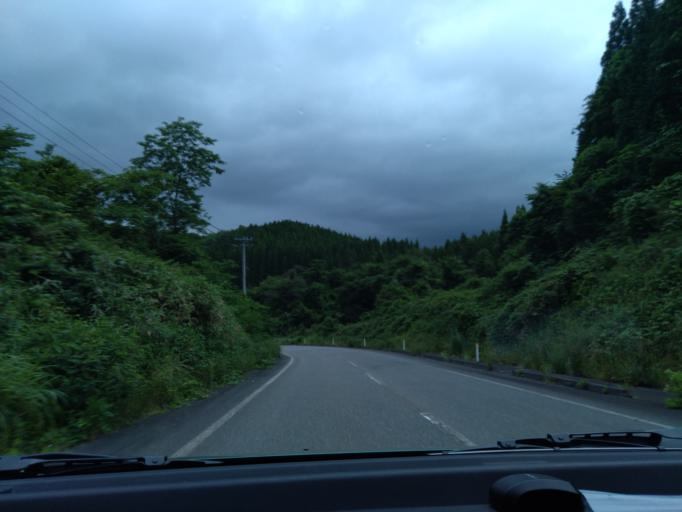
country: JP
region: Miyagi
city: Furukawa
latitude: 38.8136
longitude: 140.9066
